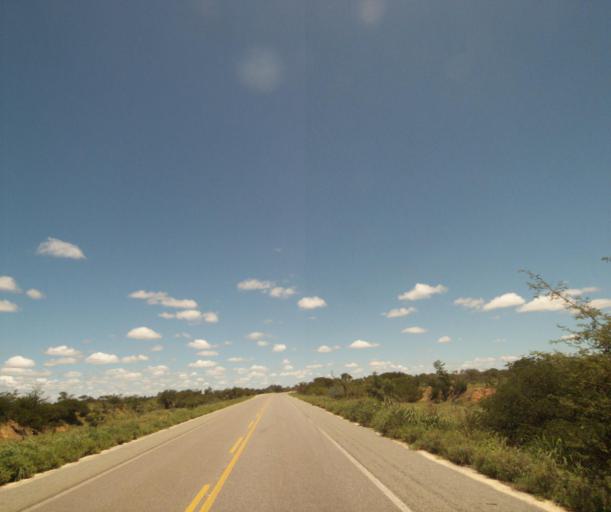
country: BR
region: Bahia
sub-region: Carinhanha
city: Carinhanha
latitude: -14.2927
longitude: -43.7856
